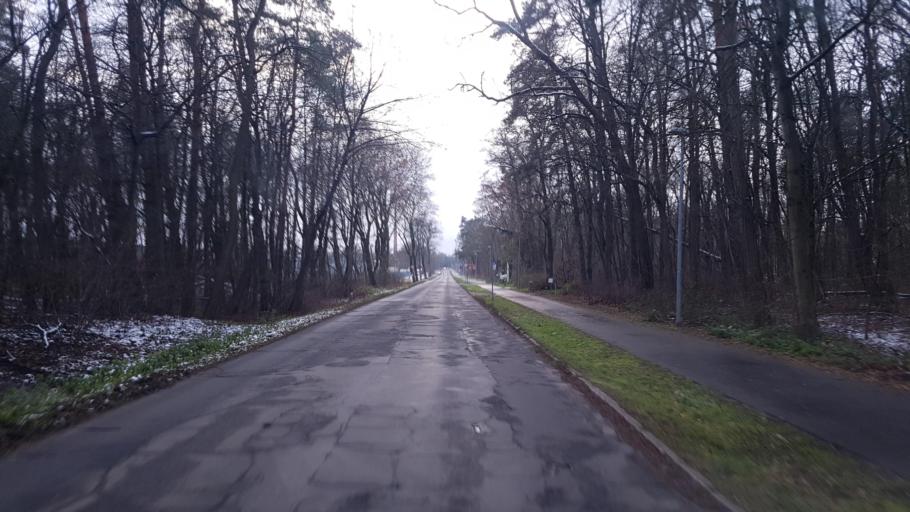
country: DE
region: Brandenburg
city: Petershagen
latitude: 52.5001
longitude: 13.8280
